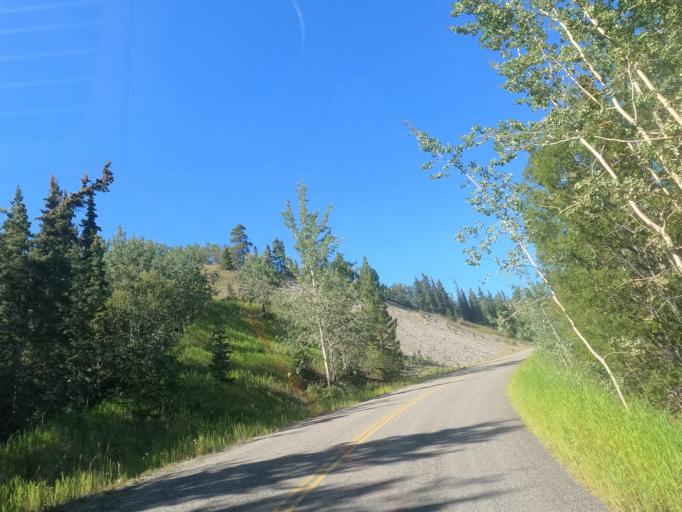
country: CA
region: Yukon
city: Whitehorse
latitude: 60.6652
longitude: -135.0364
